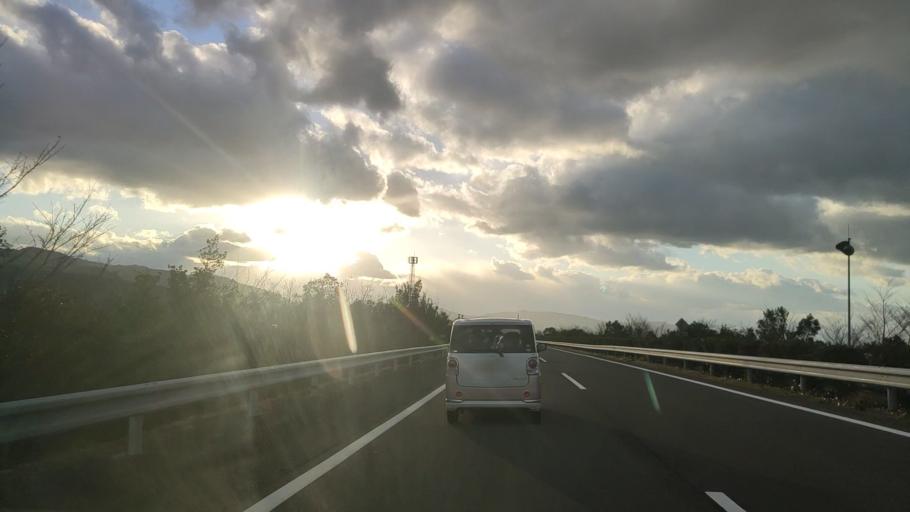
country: JP
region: Ehime
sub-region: Shikoku-chuo Shi
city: Matsuyama
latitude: 33.7880
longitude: 132.8798
